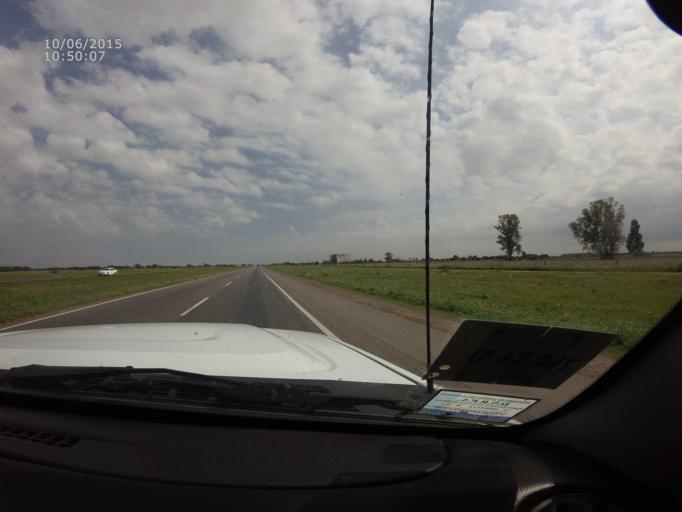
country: AR
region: Buenos Aires
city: San Nicolas de los Arroyos
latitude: -33.3781
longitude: -60.2364
